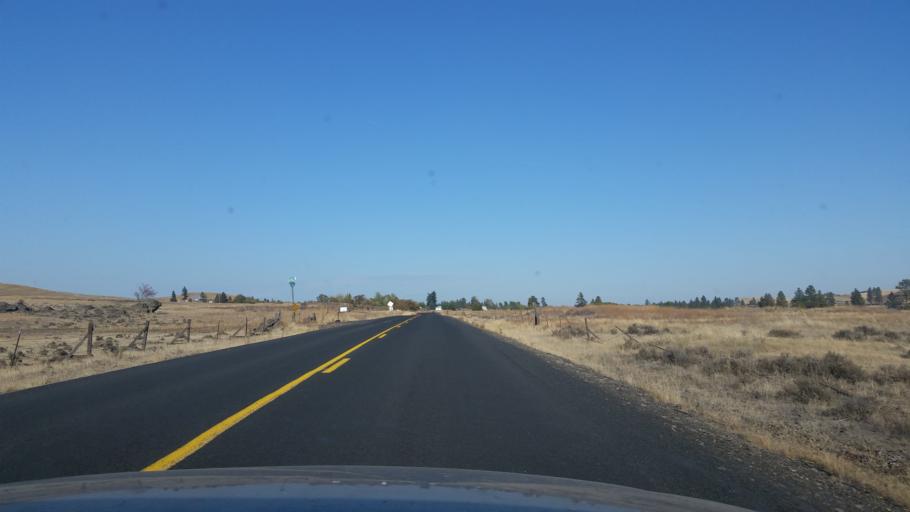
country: US
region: Washington
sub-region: Spokane County
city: Cheney
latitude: 47.3479
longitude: -117.7239
